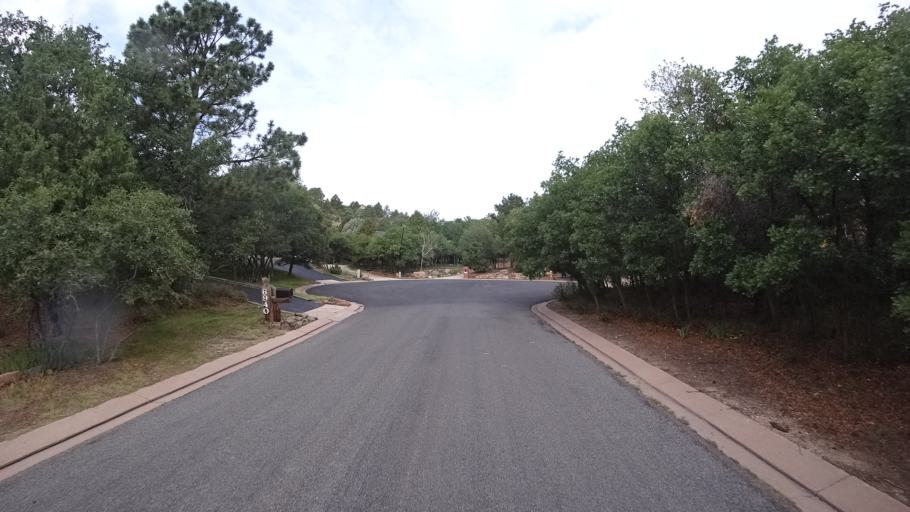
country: US
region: Colorado
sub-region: El Paso County
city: Air Force Academy
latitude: 38.9312
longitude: -104.8510
